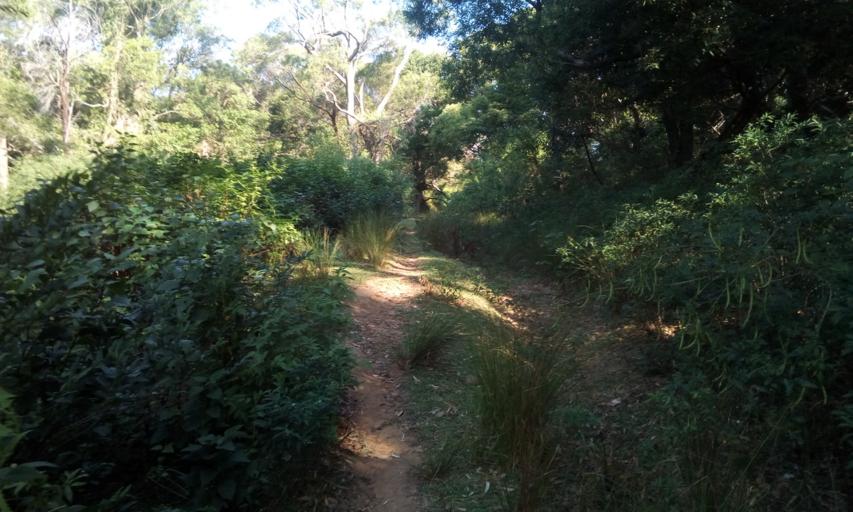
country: AU
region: New South Wales
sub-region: Wollongong
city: Mount Ousley
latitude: -34.4004
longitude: 150.8636
